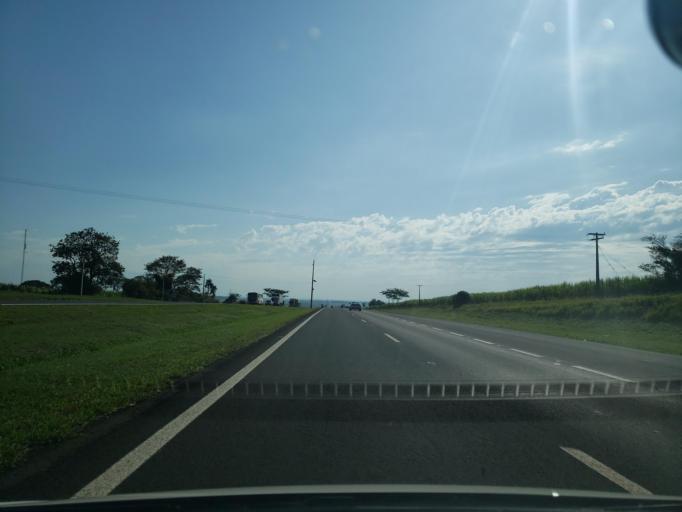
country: BR
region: Sao Paulo
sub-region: Penapolis
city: Penapolis
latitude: -21.5103
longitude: -50.0188
